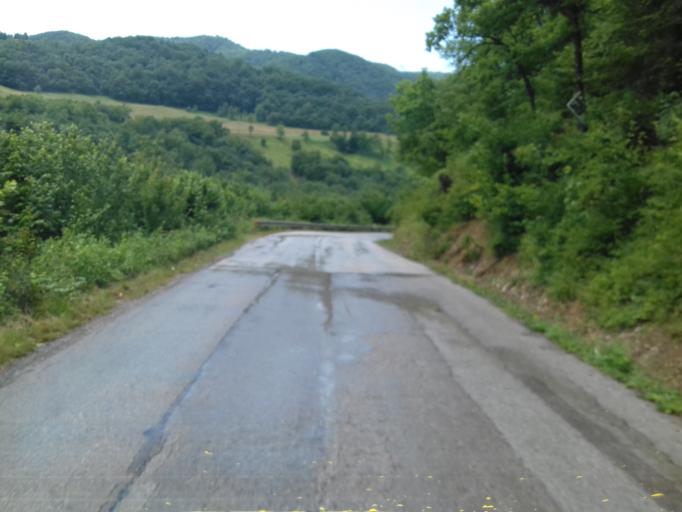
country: BA
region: Federation of Bosnia and Herzegovina
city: Kiseljak
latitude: 43.9529
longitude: 18.1331
